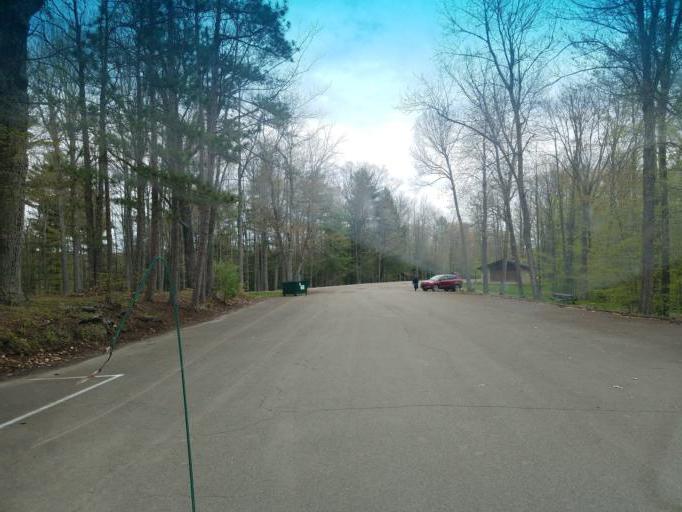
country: US
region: Pennsylvania
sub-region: Tioga County
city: Wellsboro
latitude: 41.6966
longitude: -77.4545
